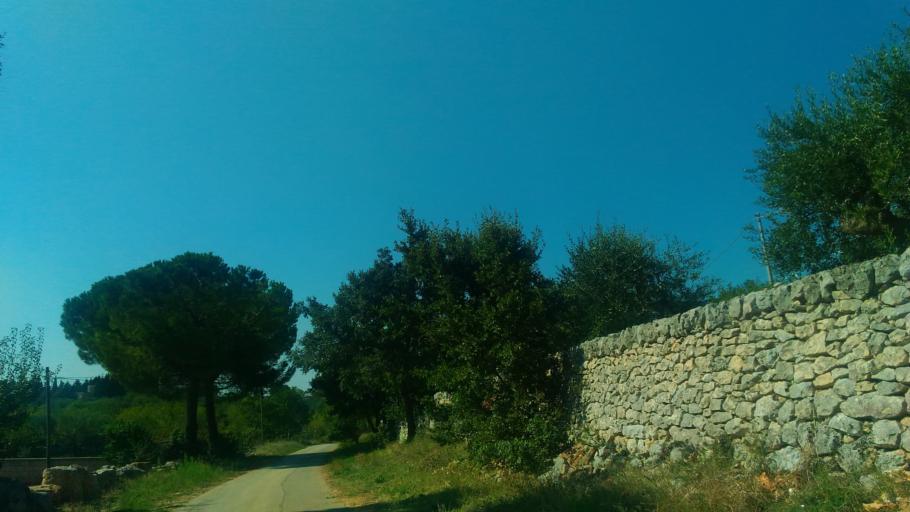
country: IT
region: Apulia
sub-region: Provincia di Bari
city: Noci
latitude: 40.8207
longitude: 17.1743
